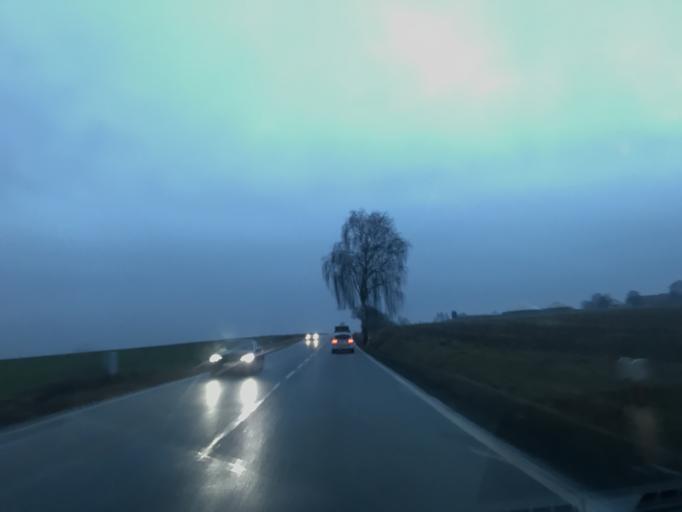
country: DE
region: Hesse
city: Grebenstein
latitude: 51.4713
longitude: 9.4013
